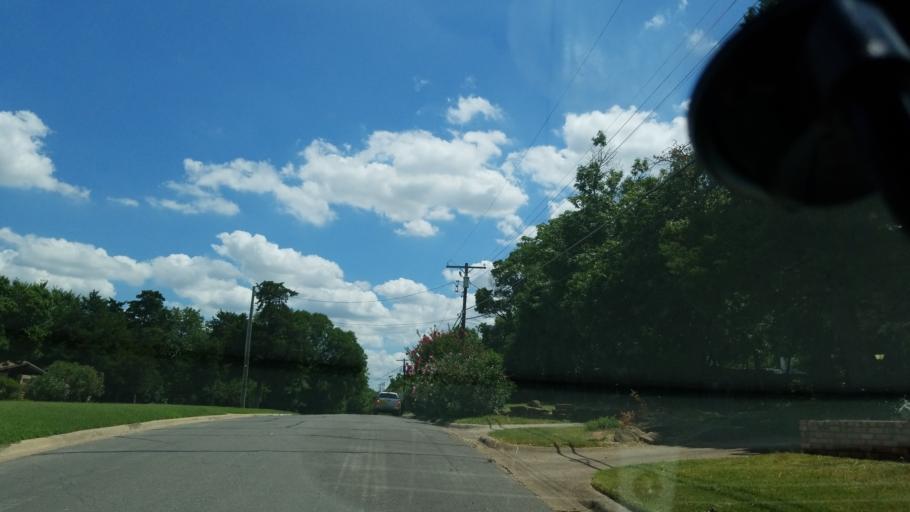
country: US
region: Texas
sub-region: Dallas County
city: Cockrell Hill
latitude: 32.7038
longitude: -96.8702
